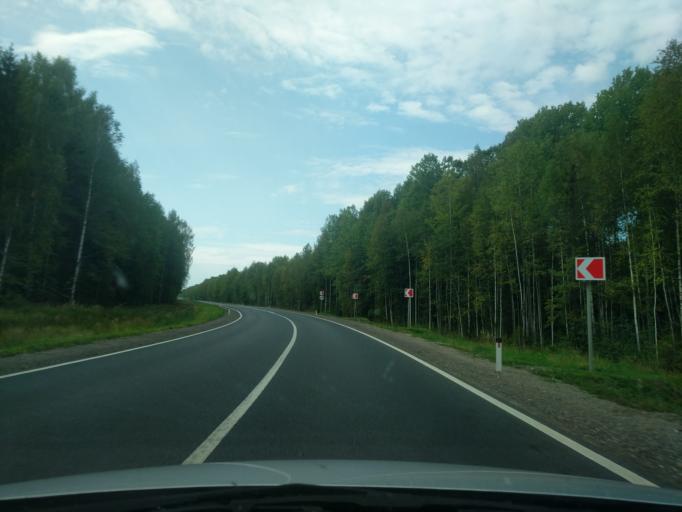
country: RU
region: Kostroma
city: Kadyy
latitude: 57.8528
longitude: 43.4927
